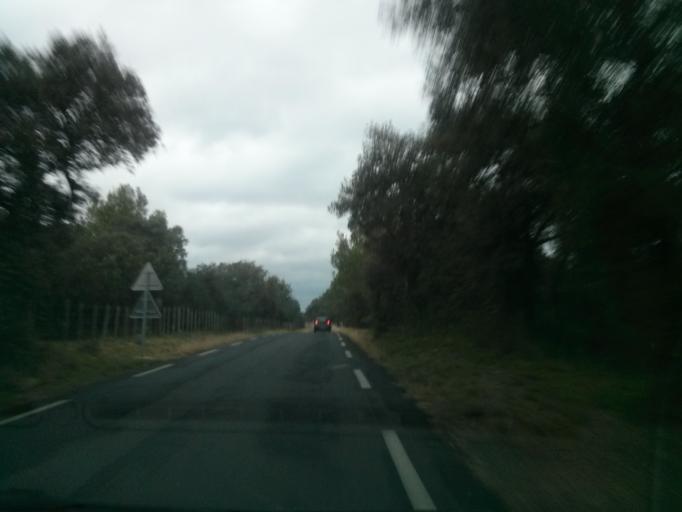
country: FR
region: Languedoc-Roussillon
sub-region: Departement de l'Herault
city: Boisseron
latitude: 43.7587
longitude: 4.1119
